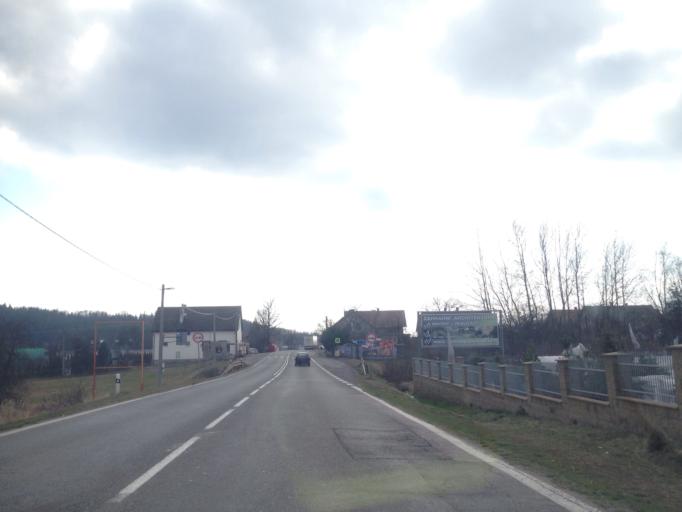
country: CZ
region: Kralovehradecky
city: Nova Paka
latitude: 50.4712
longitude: 15.4996
